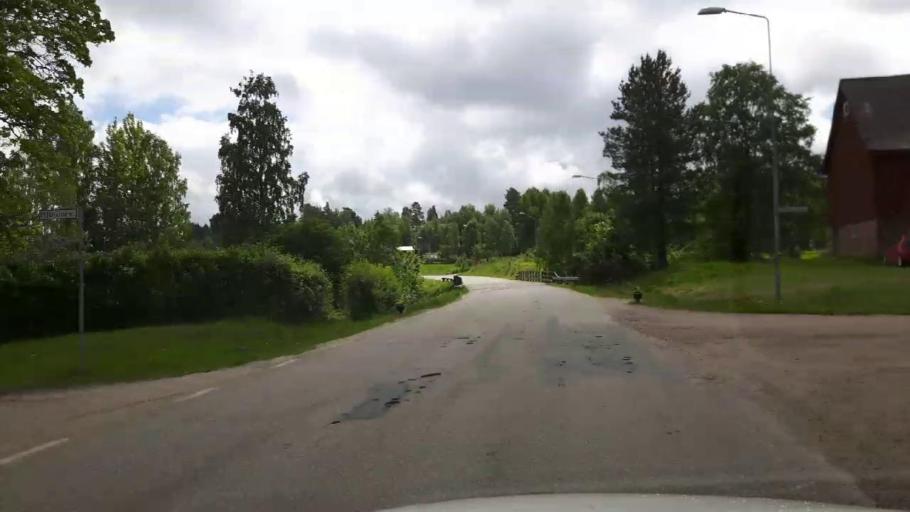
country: SE
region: Gaevleborg
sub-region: Ovanakers Kommun
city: Alfta
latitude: 61.3371
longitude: 15.9583
